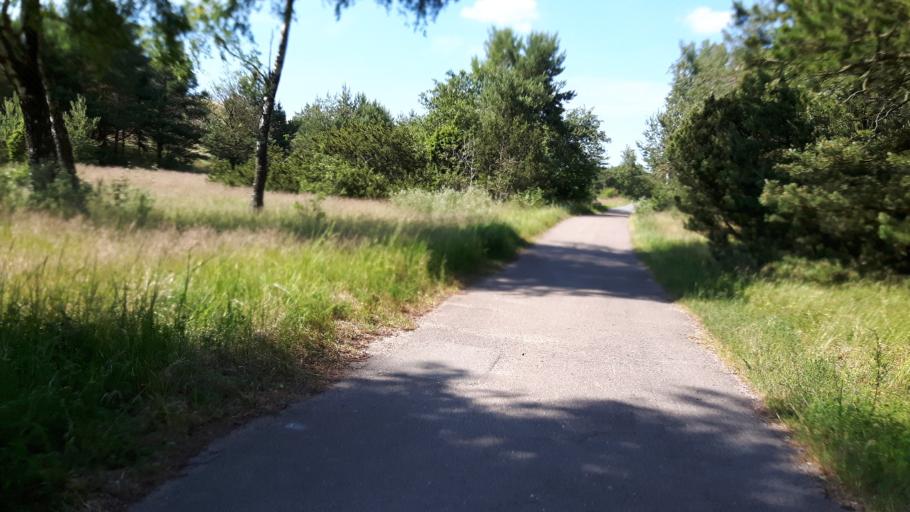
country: LT
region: Klaipedos apskritis
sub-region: Klaipeda
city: Klaipeda
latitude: 55.6837
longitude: 21.1042
